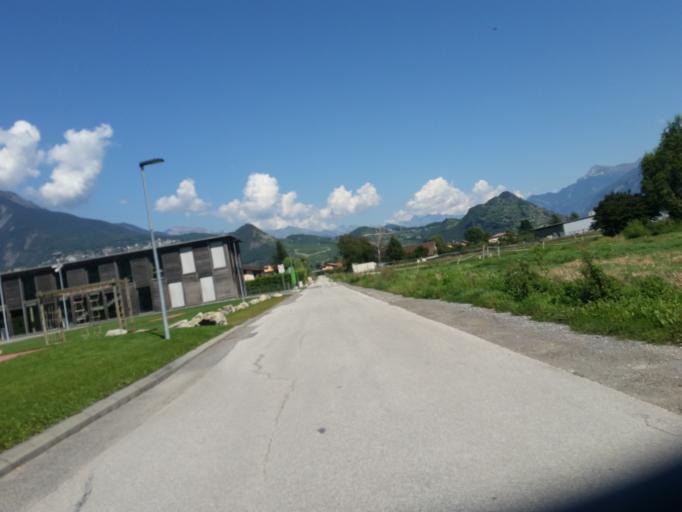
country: CH
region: Valais
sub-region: Conthey District
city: Vetroz
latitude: 46.2189
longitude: 7.2812
